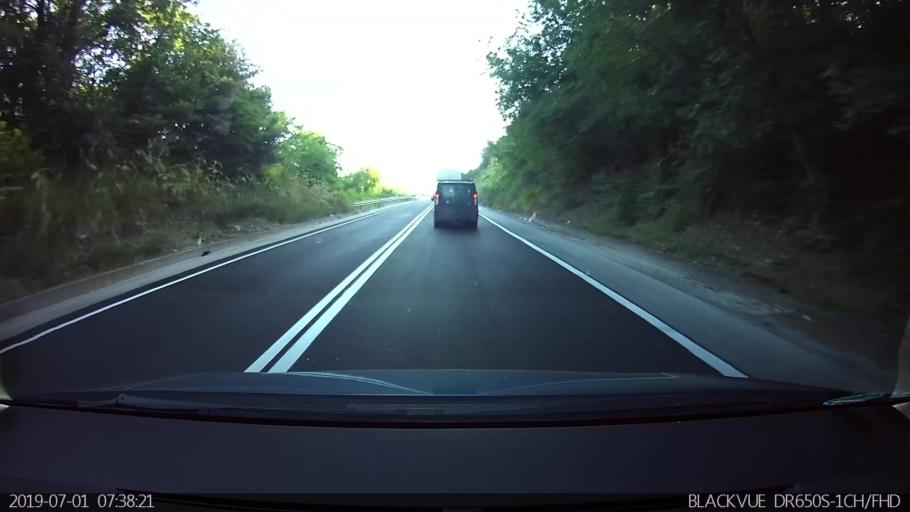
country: IT
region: Latium
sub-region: Provincia di Frosinone
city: Giuliano di Roma
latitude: 41.5432
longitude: 13.2686
